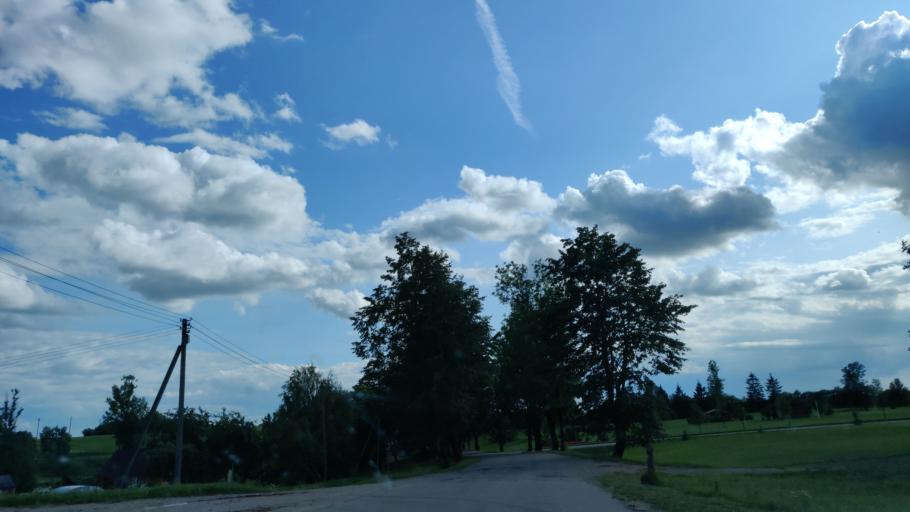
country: LT
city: Varniai
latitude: 55.5936
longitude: 22.3089
